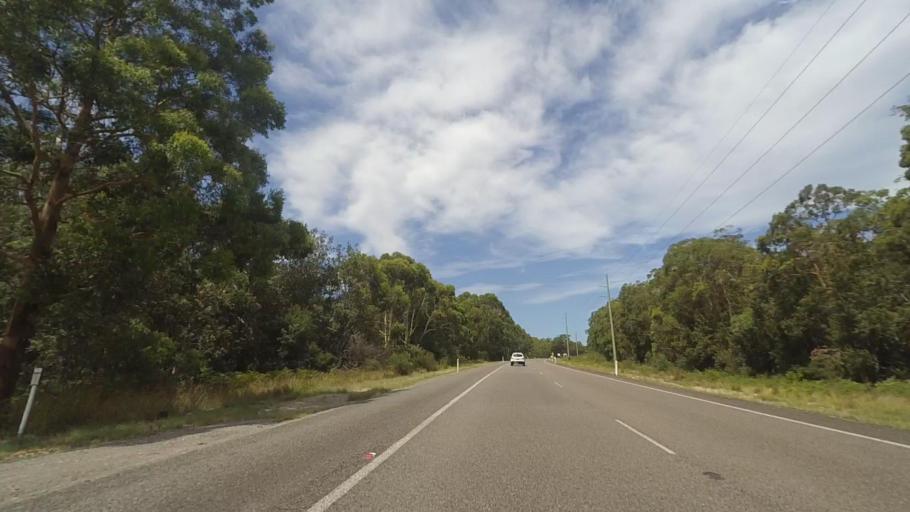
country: AU
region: New South Wales
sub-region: Port Stephens Shire
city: Medowie
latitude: -32.7866
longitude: 151.9663
